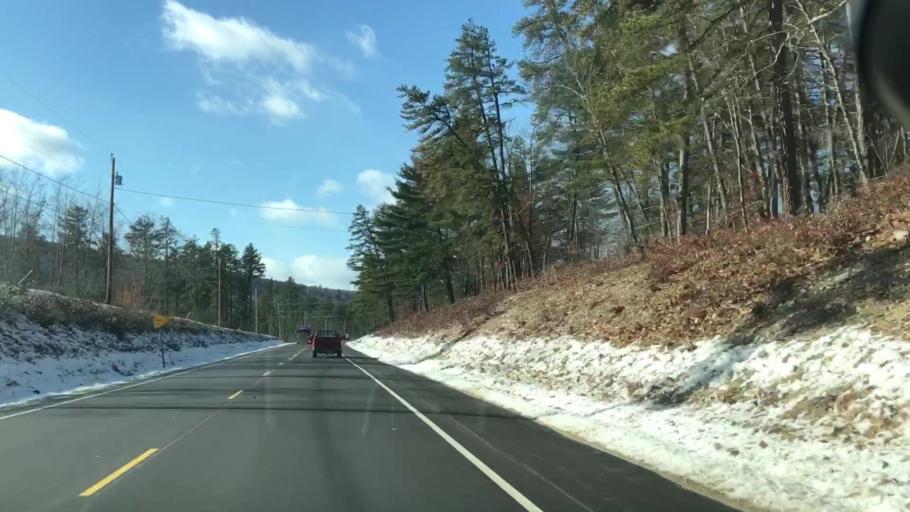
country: US
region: New Hampshire
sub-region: Carroll County
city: Freedom
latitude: 43.7948
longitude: -71.0171
